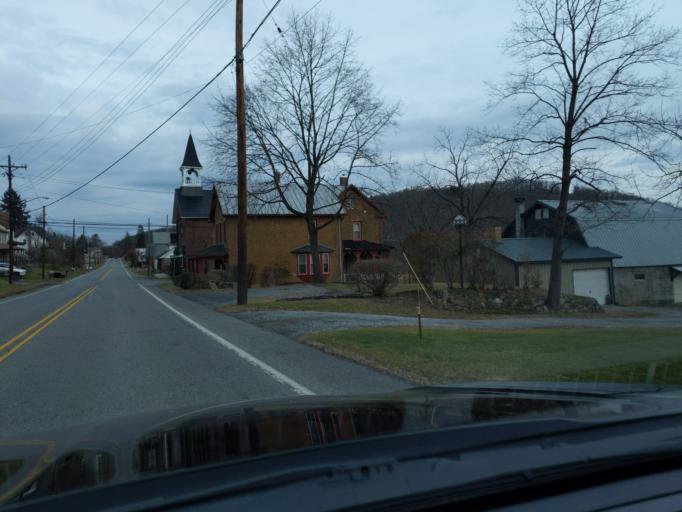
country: US
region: Pennsylvania
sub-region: Blair County
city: Hollidaysburg
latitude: 40.4483
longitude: -78.3468
